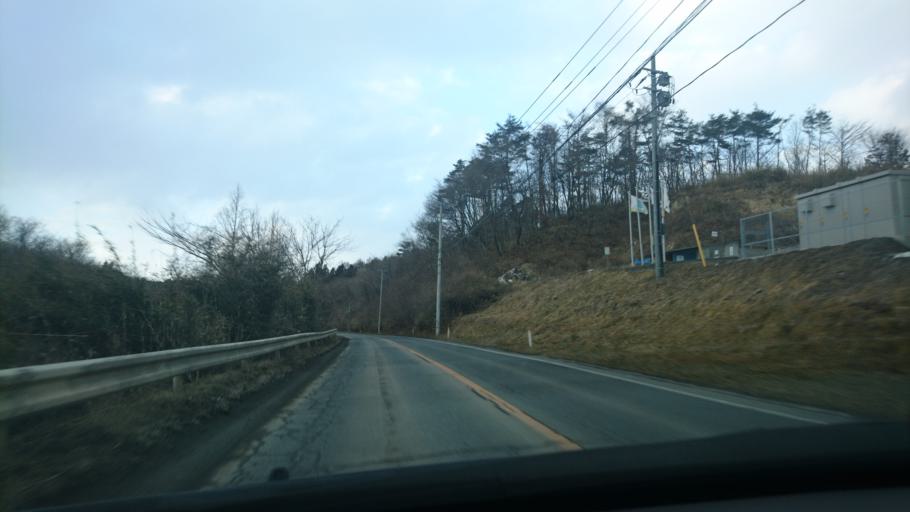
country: JP
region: Iwate
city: Ichinoseki
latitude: 38.9682
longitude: 141.3320
